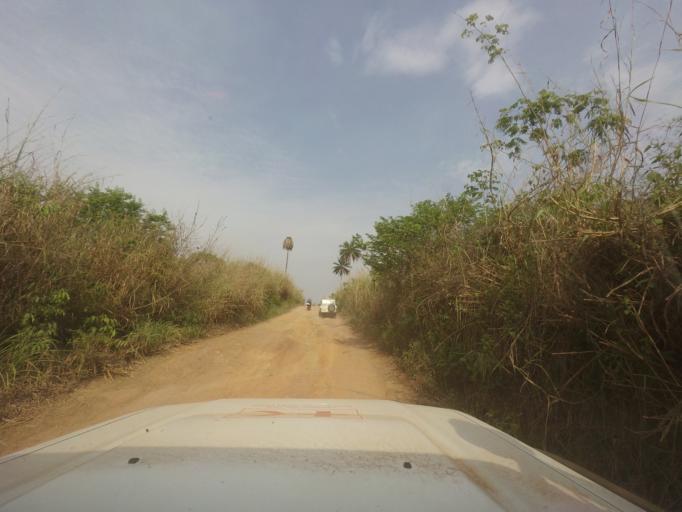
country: GN
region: Nzerekore
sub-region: Prefecture de Guekedou
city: Gueckedou
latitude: 8.5232
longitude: -10.2124
